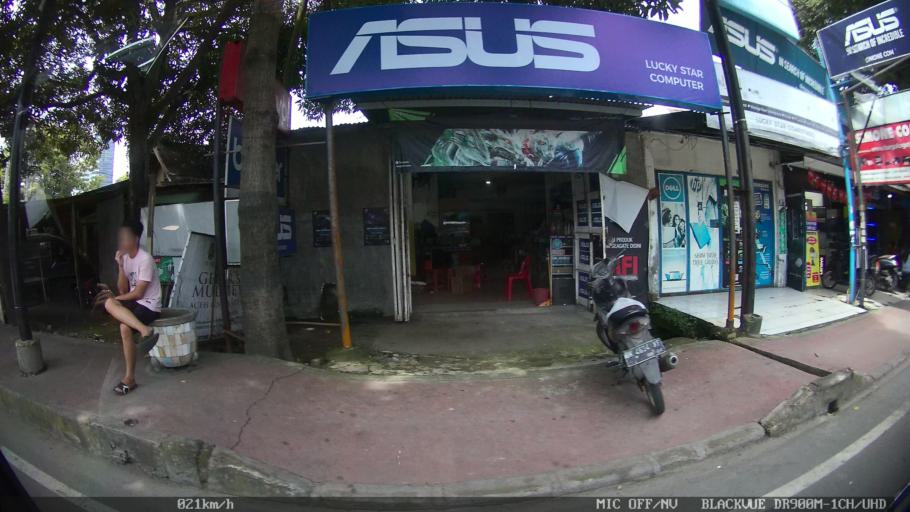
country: ID
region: North Sumatra
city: Medan
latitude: 3.6000
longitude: 98.6744
